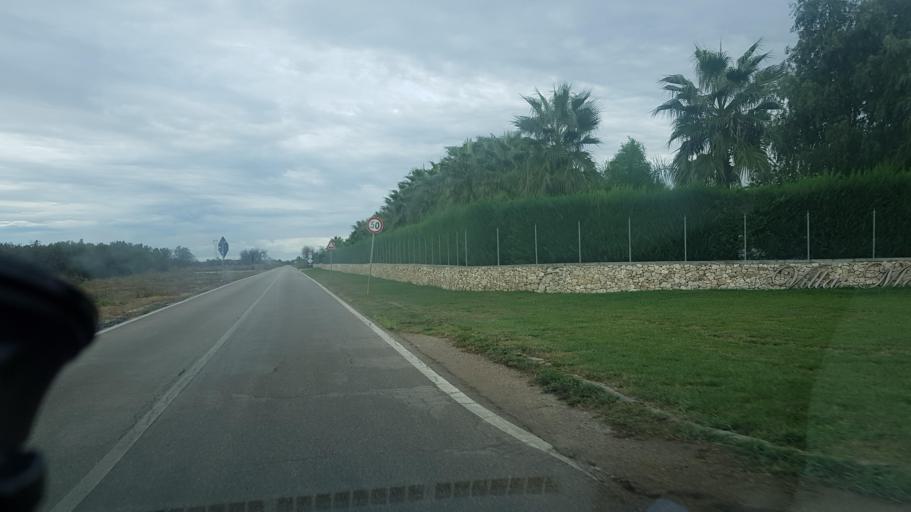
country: IT
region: Apulia
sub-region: Provincia di Lecce
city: Campi Salentina
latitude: 40.3635
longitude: 18.0081
